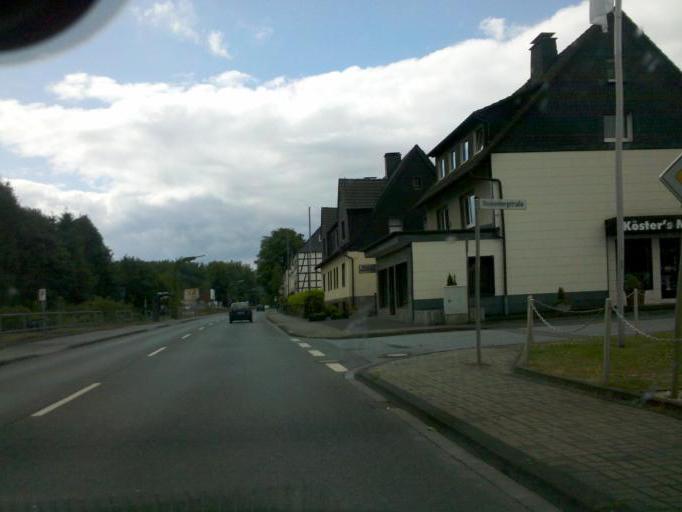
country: DE
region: North Rhine-Westphalia
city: Warstein
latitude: 51.4778
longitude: 8.3367
